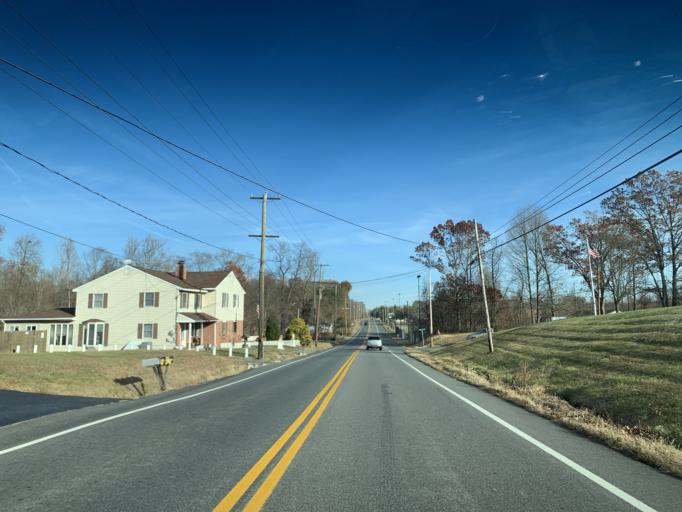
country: US
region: Maryland
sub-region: Cecil County
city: Elkton
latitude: 39.6056
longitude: -75.8673
